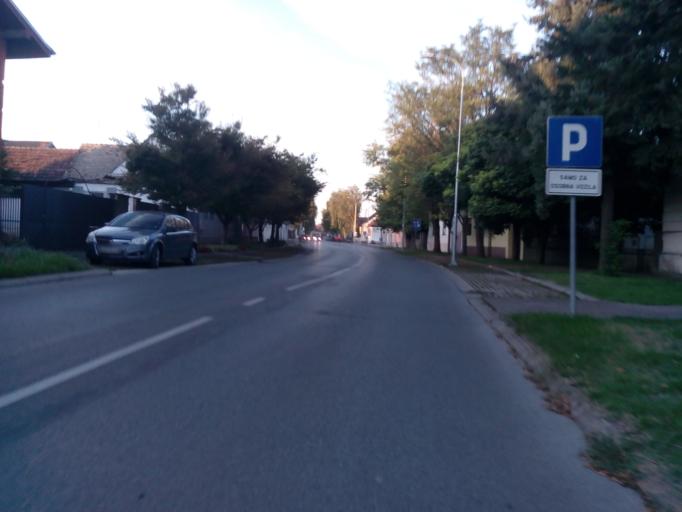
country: HR
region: Vukovarsko-Srijemska
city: Vinkovci
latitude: 45.2904
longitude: 18.8106
